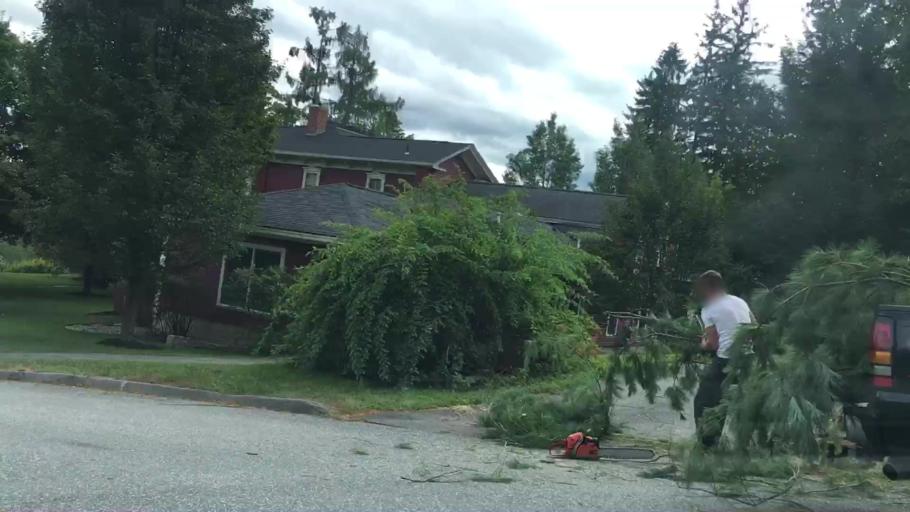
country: US
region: Maine
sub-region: Kennebec County
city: Hallowell
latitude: 44.2871
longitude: -69.7964
